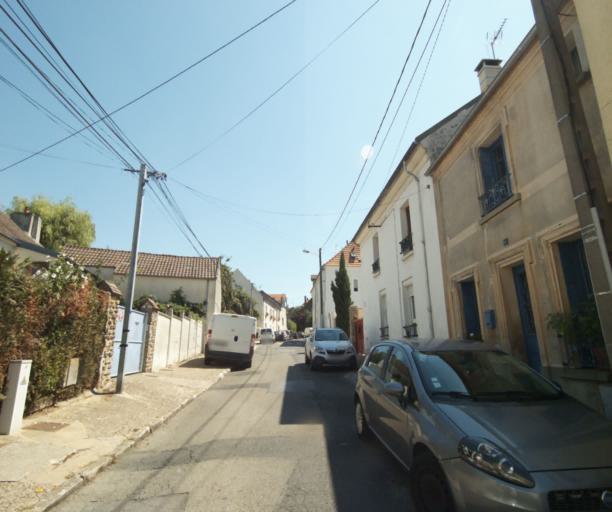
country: FR
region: Ile-de-France
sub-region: Departement de Seine-et-Marne
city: Montevrain
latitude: 48.8753
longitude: 2.7436
